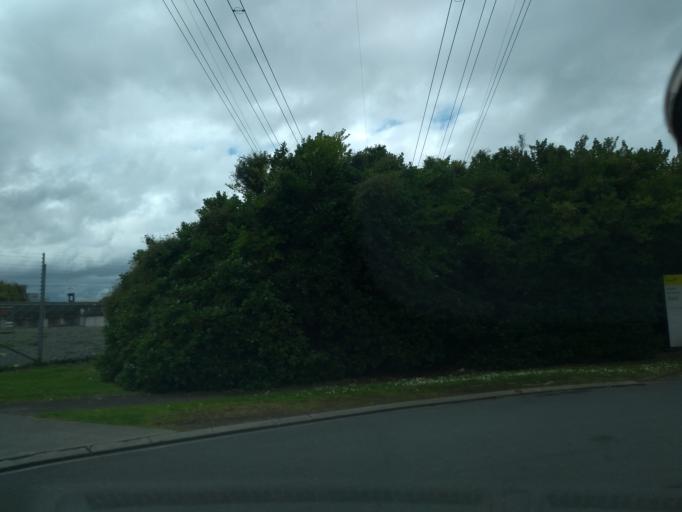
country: NZ
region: Auckland
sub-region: Auckland
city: Mangere
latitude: -36.9273
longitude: 174.8262
